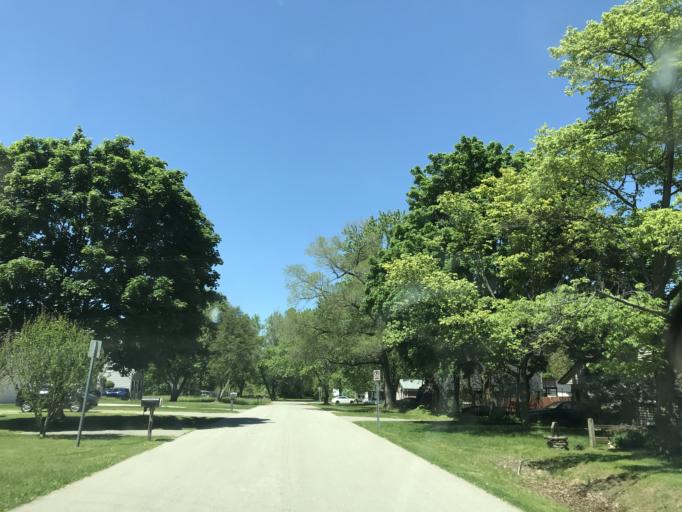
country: US
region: Michigan
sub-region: Wayne County
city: Woodhaven
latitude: 42.1756
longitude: -83.2999
